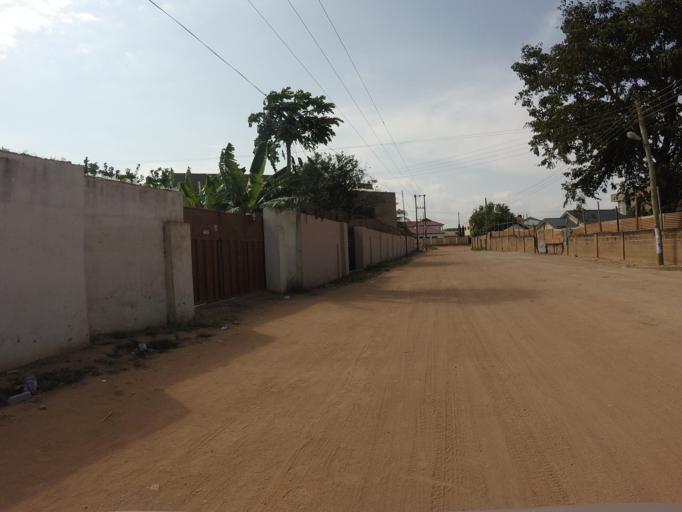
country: GH
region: Greater Accra
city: Dome
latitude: 5.6391
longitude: -0.2345
